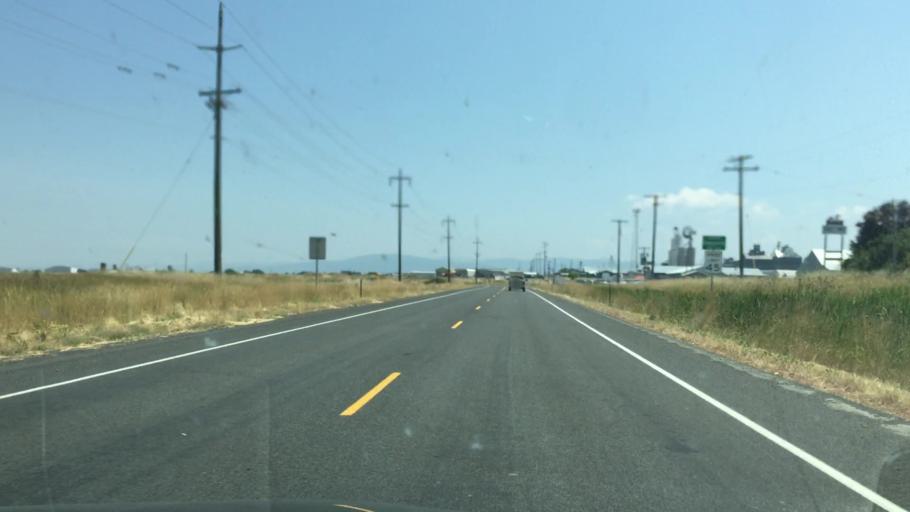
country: US
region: Idaho
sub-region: Idaho County
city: Grangeville
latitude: 45.9361
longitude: -116.1393
